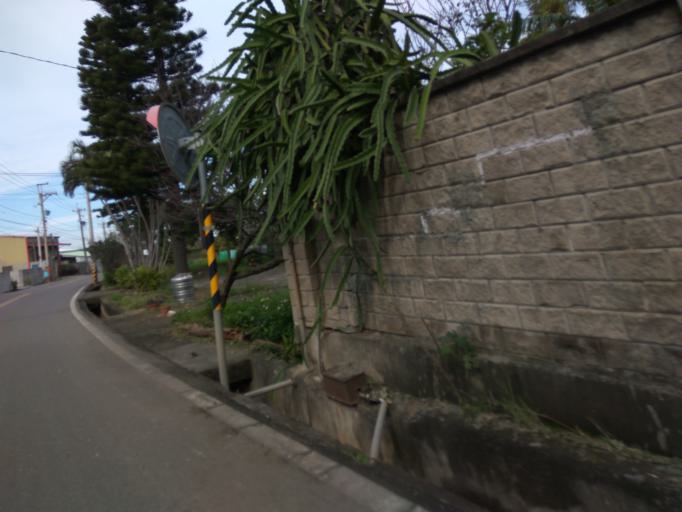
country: TW
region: Taiwan
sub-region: Hsinchu
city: Zhubei
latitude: 24.9609
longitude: 121.0991
